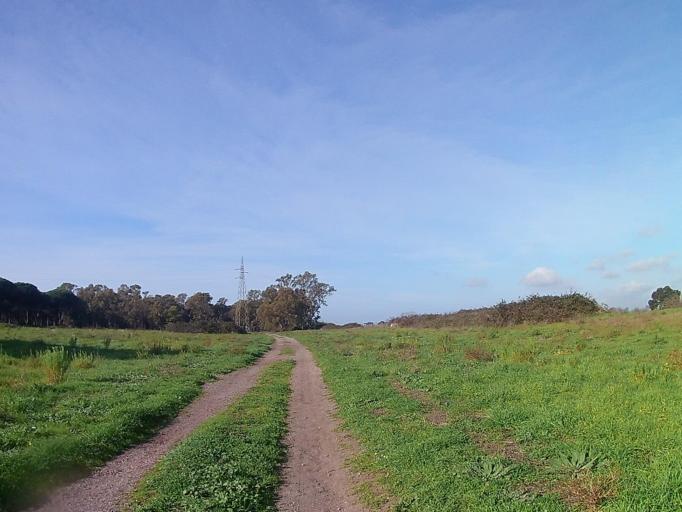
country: IT
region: Latium
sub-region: Citta metropolitana di Roma Capitale
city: Lido di Ostia
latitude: 41.7446
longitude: 12.2847
